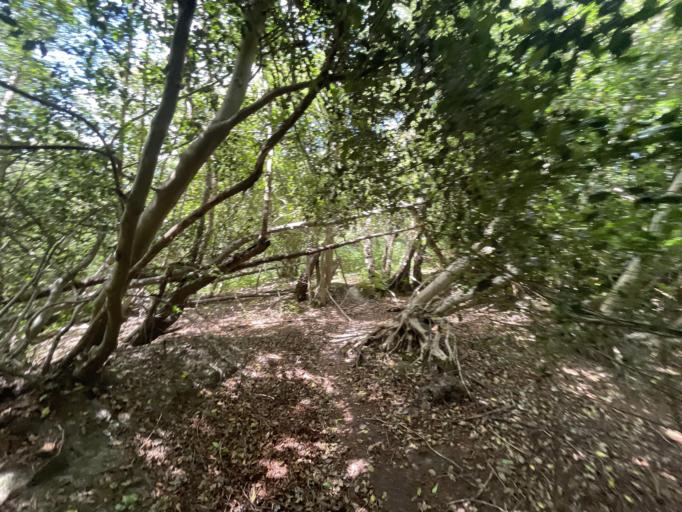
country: GB
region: England
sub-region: Kent
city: Edenbridge
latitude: 51.1641
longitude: 0.1346
